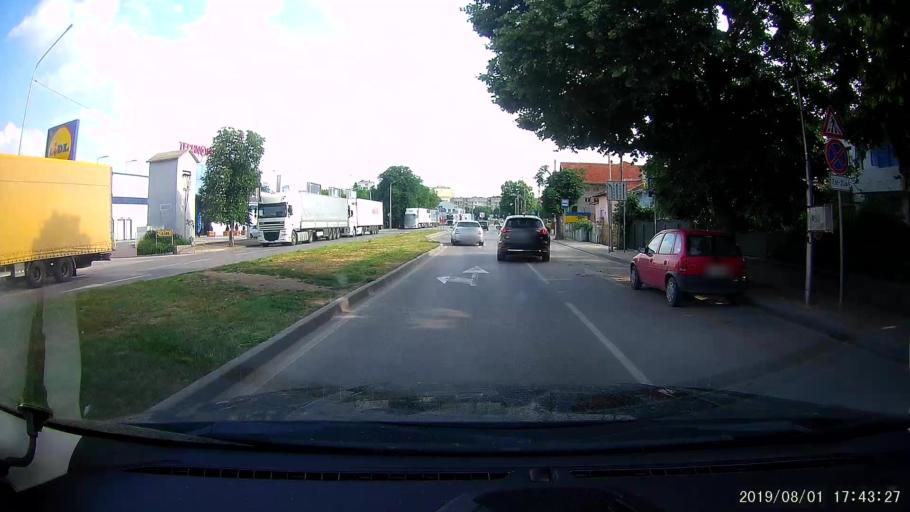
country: BG
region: Silistra
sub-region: Obshtina Silistra
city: Silistra
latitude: 44.1147
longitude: 27.2728
